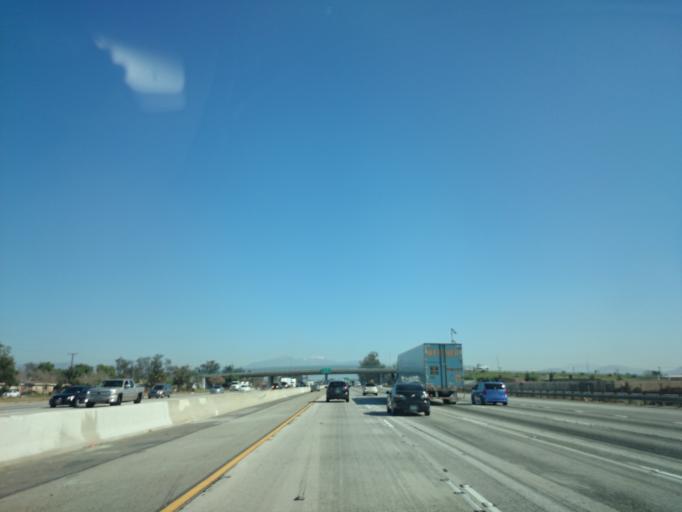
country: US
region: California
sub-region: San Bernardino County
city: Fontana
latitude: 34.0668
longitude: -117.4481
